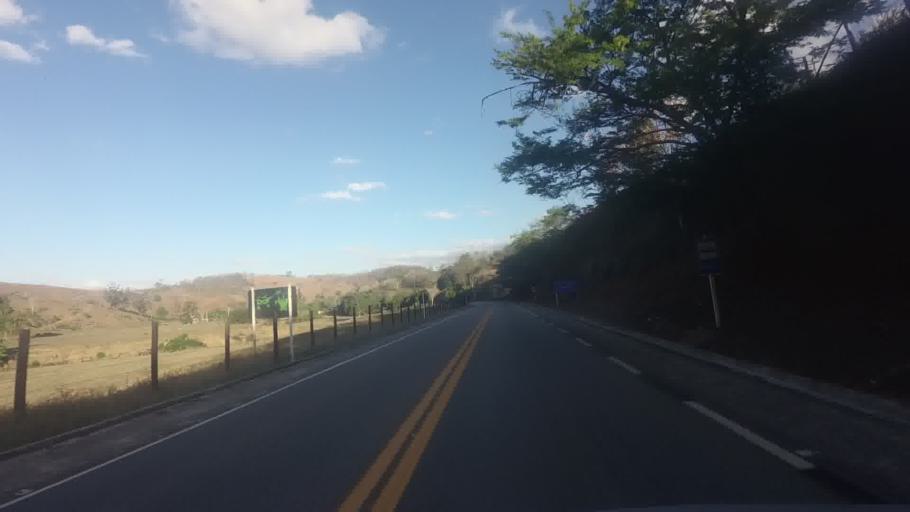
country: BR
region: Espirito Santo
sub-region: Cachoeiro De Itapemirim
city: Cachoeiro de Itapemirim
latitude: -20.8265
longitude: -41.2151
